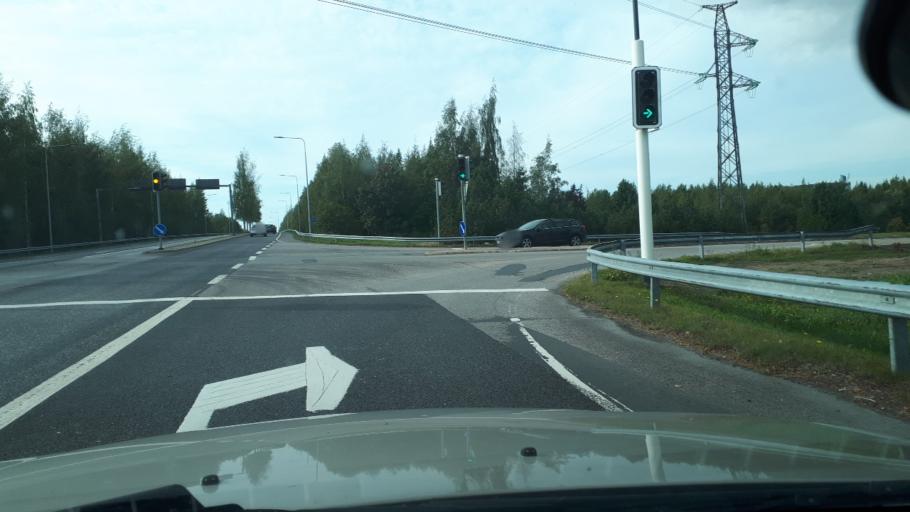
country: FI
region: Northern Ostrobothnia
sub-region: Oulu
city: Oulu
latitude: 65.0561
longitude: 25.4424
